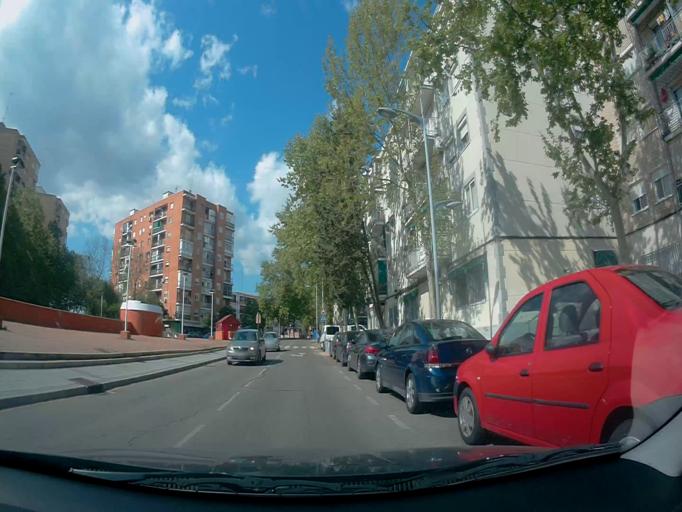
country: ES
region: Madrid
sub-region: Provincia de Madrid
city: Alcorcon
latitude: 40.3462
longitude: -3.8333
